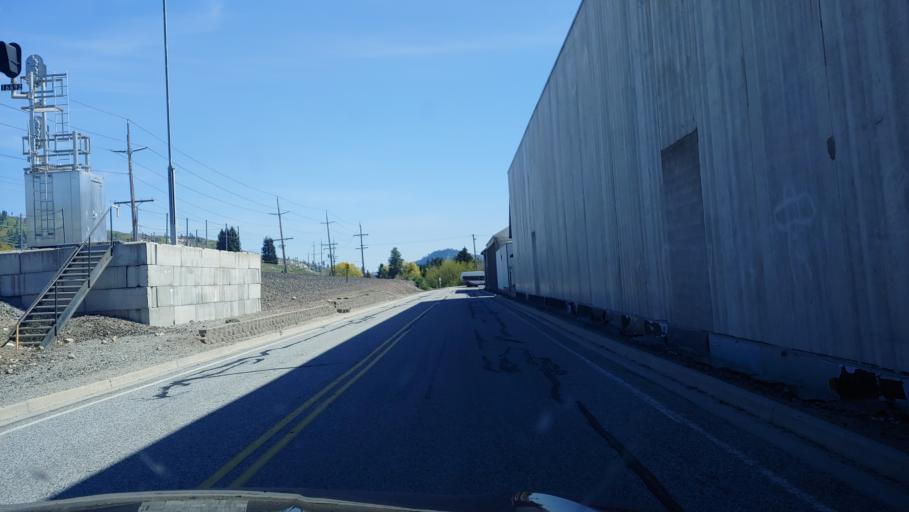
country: US
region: Washington
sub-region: Chelan County
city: Leavenworth
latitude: 47.5727
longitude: -120.6054
